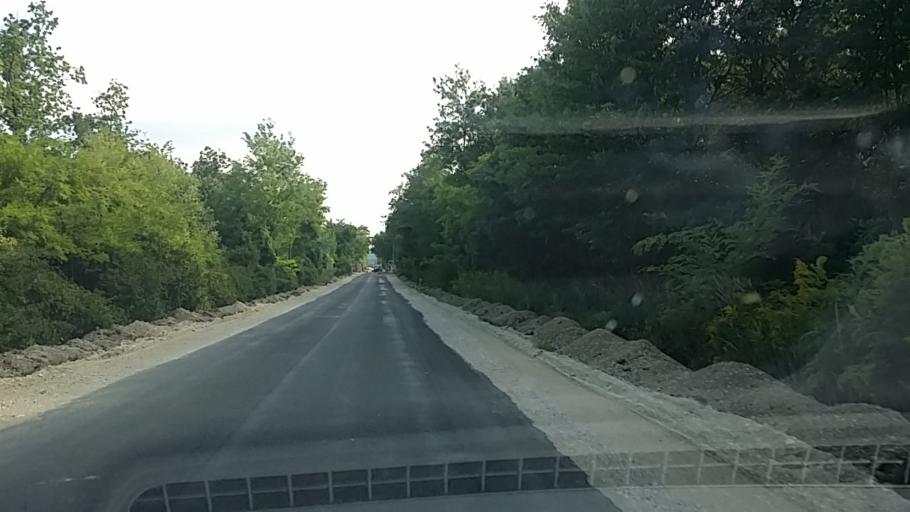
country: AT
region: Burgenland
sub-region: Eisenstadt-Umgebung
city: Morbisch am See
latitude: 47.7591
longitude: 16.6225
